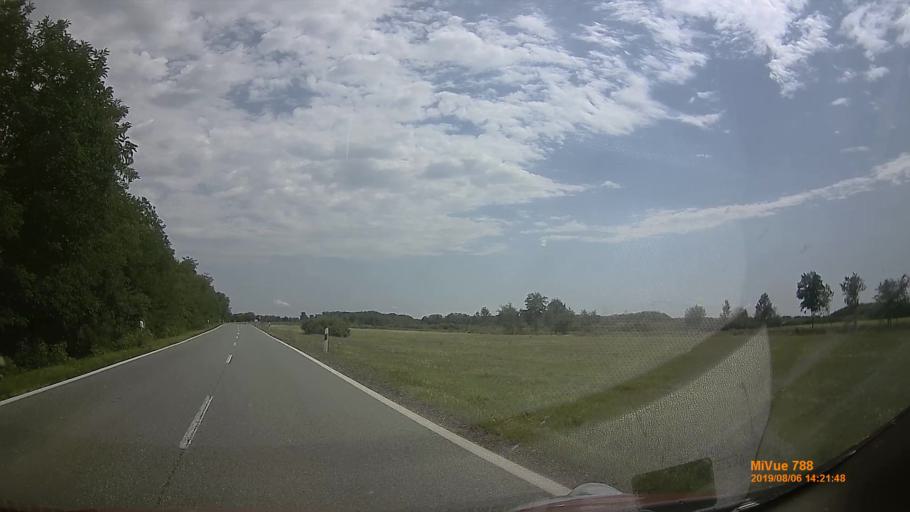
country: HU
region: Vas
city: Vep
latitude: 47.1677
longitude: 16.7813
